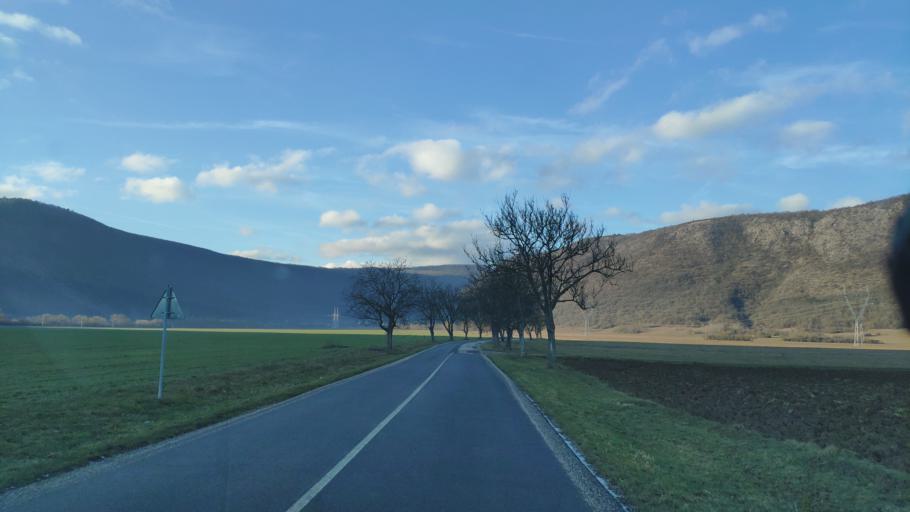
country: SK
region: Kosicky
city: Medzev
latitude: 48.6151
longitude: 20.8802
